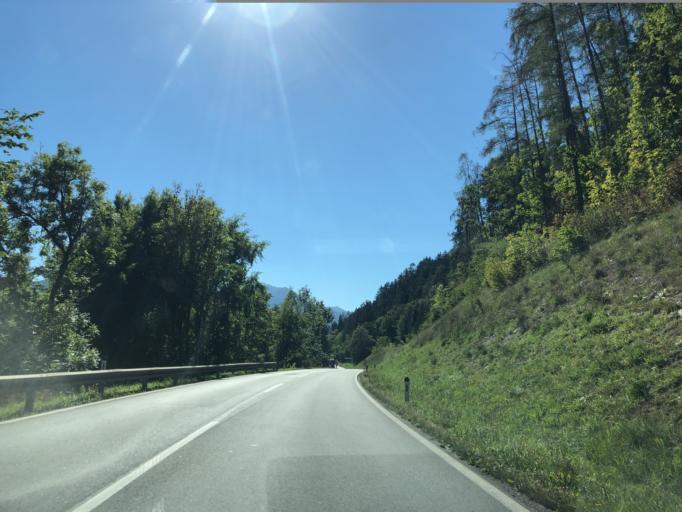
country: AT
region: Tyrol
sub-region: Politischer Bezirk Imst
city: Tarrenz
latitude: 47.2575
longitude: 10.7534
